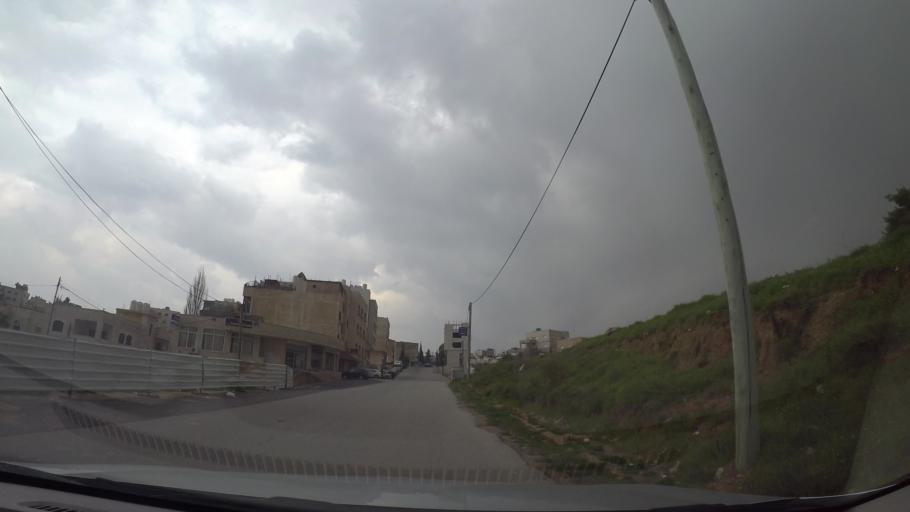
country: JO
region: Amman
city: Umm as Summaq
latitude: 31.8845
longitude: 35.8545
